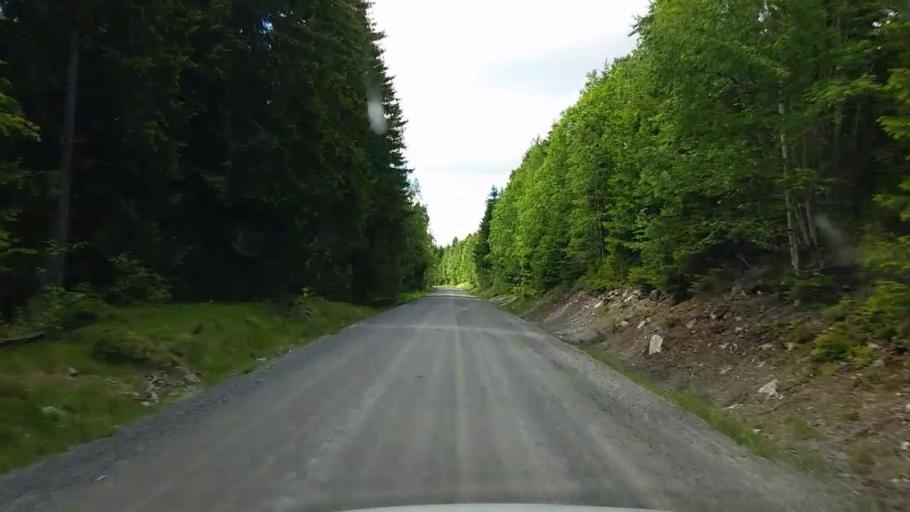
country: SE
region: Gaevleborg
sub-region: Bollnas Kommun
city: Vittsjo
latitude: 61.0919
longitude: 16.2276
